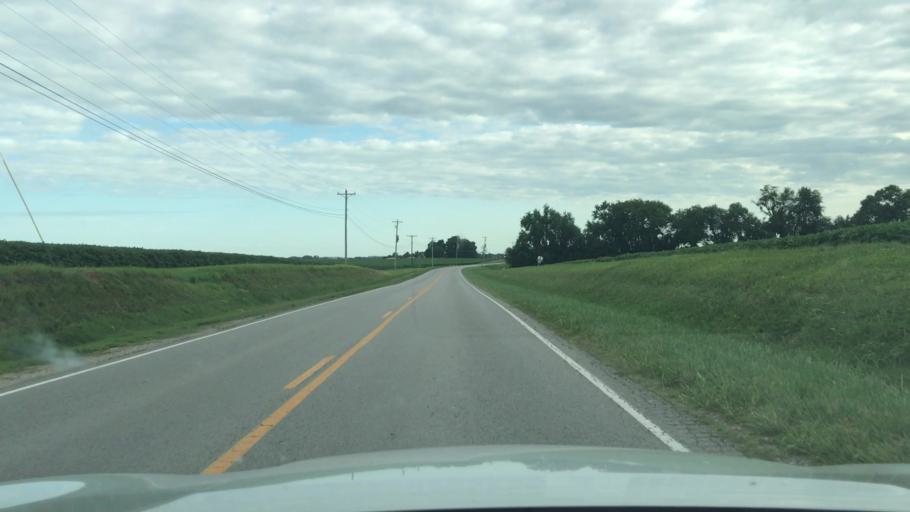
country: US
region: Kentucky
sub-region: Todd County
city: Elkton
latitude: 36.7694
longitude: -87.1668
